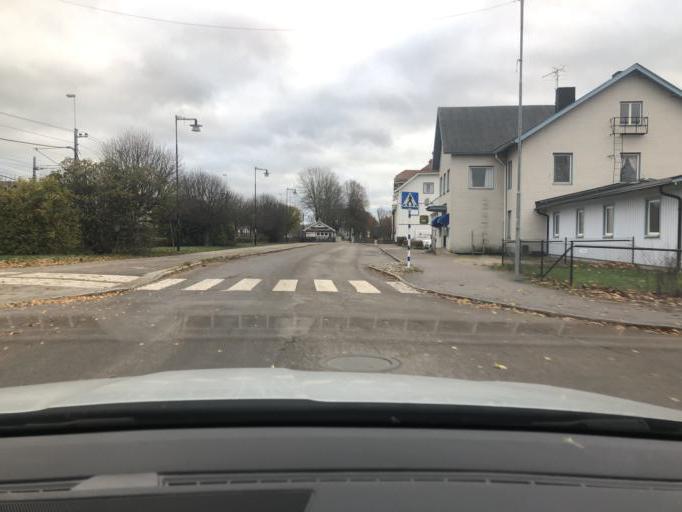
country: SE
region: Uppsala
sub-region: Tierps Kommun
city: Tierp
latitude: 60.3448
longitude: 17.5145
